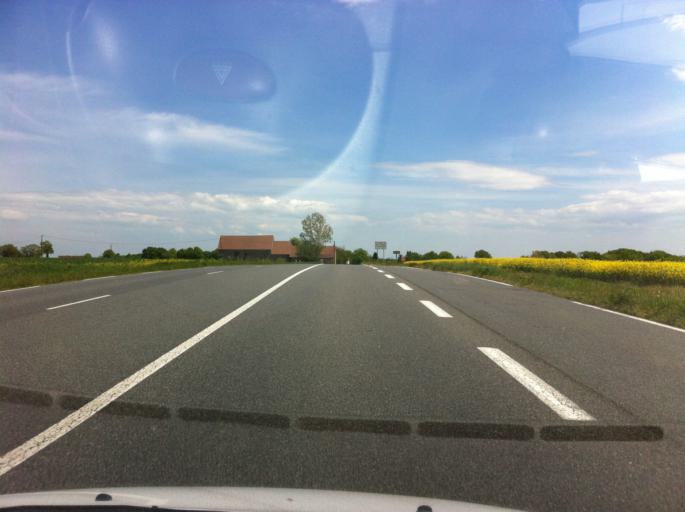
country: FR
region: Auvergne
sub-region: Departement de l'Allier
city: Chantelle
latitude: 46.3172
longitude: 3.1711
